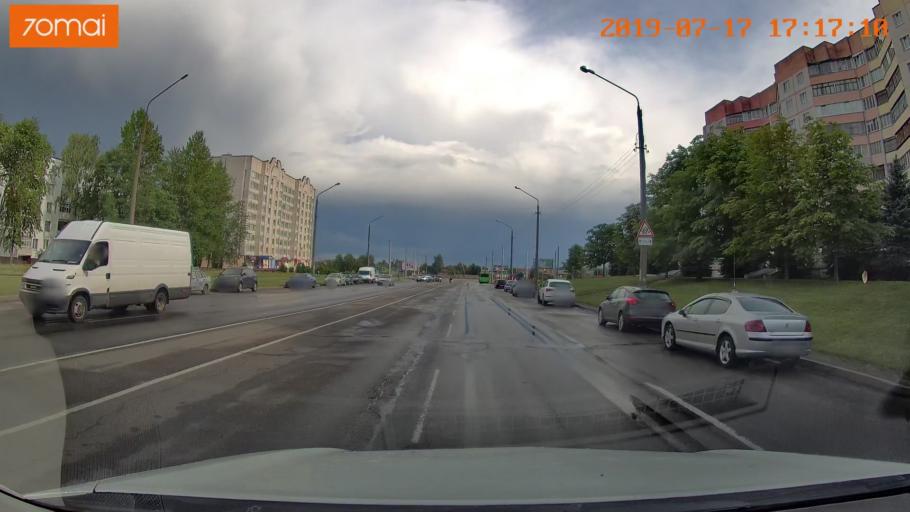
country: BY
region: Mogilev
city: Babruysk
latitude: 53.1623
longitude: 29.1979
